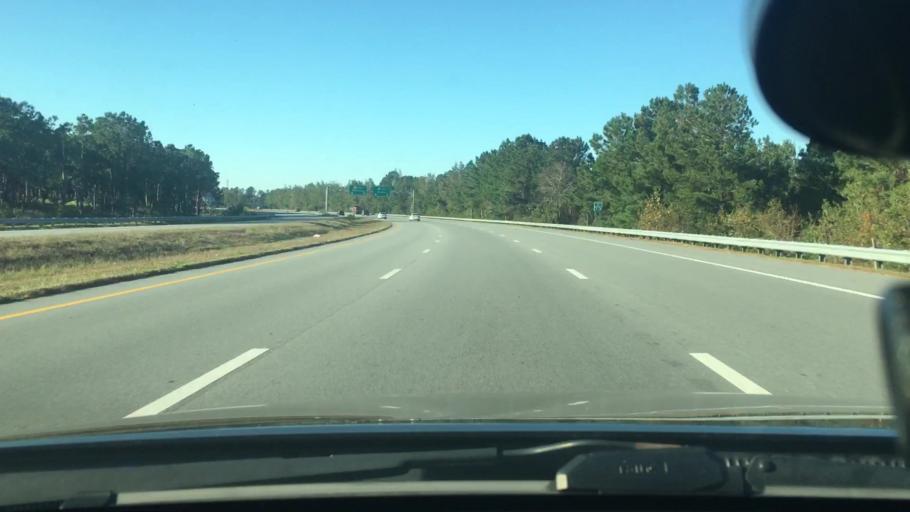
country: US
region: North Carolina
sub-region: Craven County
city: James City
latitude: 35.1093
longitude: -77.0084
